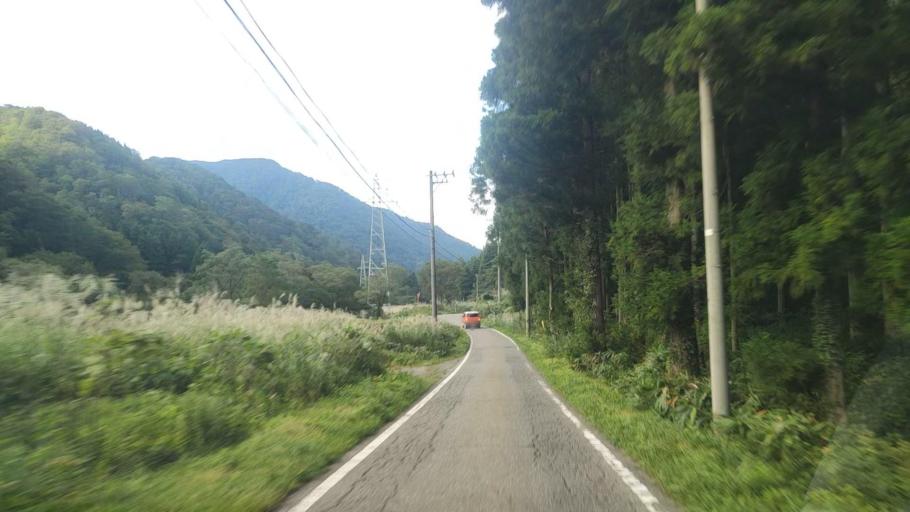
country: JP
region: Toyama
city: Yatsuomachi-higashikumisaka
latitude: 36.4445
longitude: 137.0841
